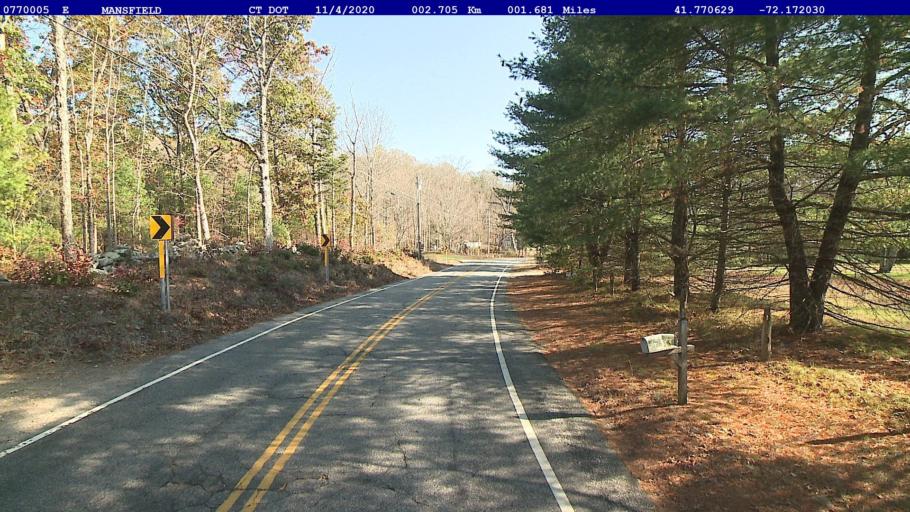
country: US
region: Connecticut
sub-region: Tolland County
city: Mansfield City
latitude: 41.7705
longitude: -72.1721
